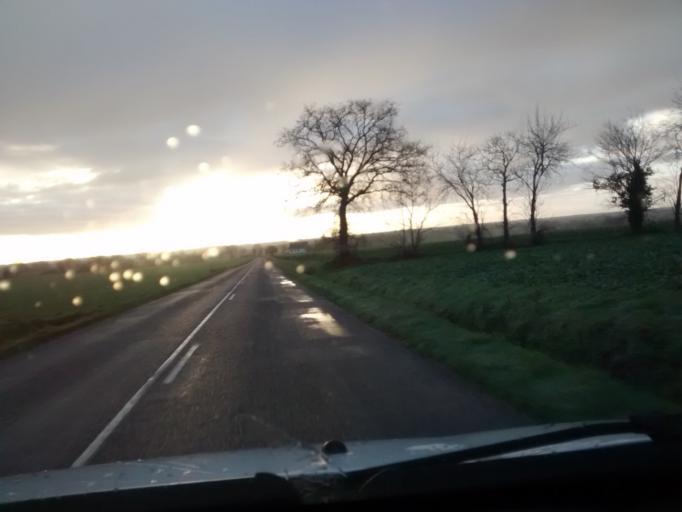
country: FR
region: Brittany
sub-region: Departement d'Ille-et-Vilaine
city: Bais
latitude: 47.9804
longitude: -1.2765
